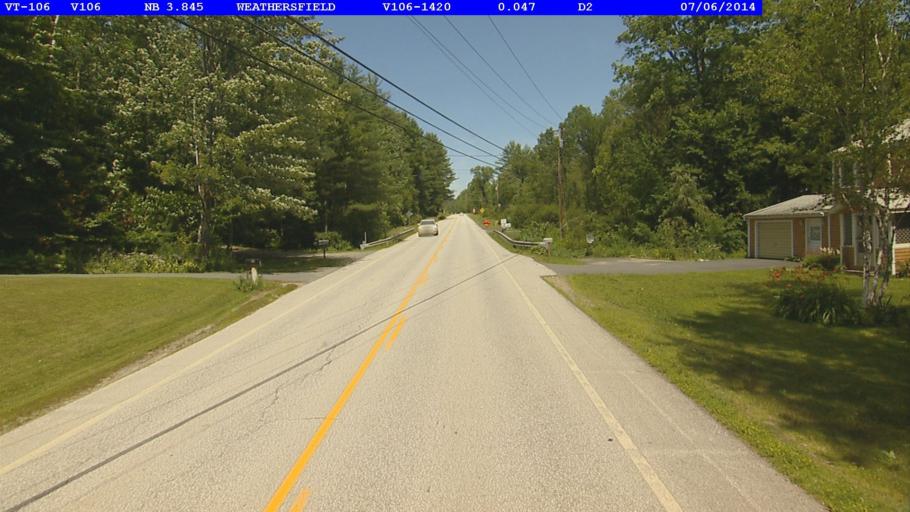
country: US
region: Vermont
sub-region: Windsor County
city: Springfield
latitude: 43.3451
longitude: -72.5307
